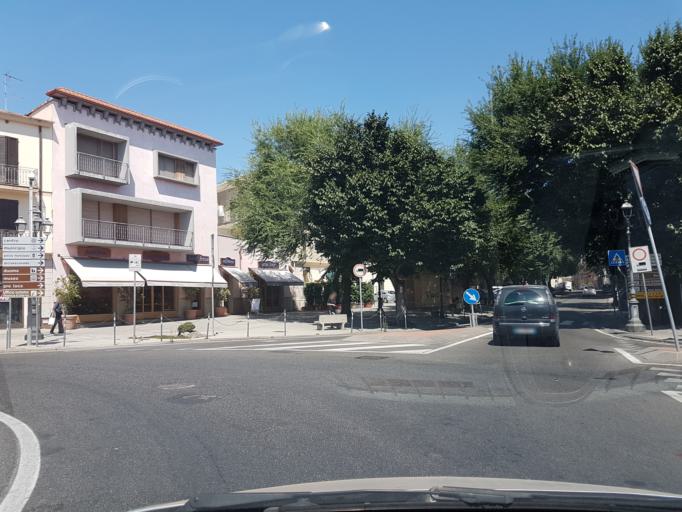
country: IT
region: Sardinia
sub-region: Provincia di Oristano
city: Oristano
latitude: 39.9007
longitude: 8.5919
